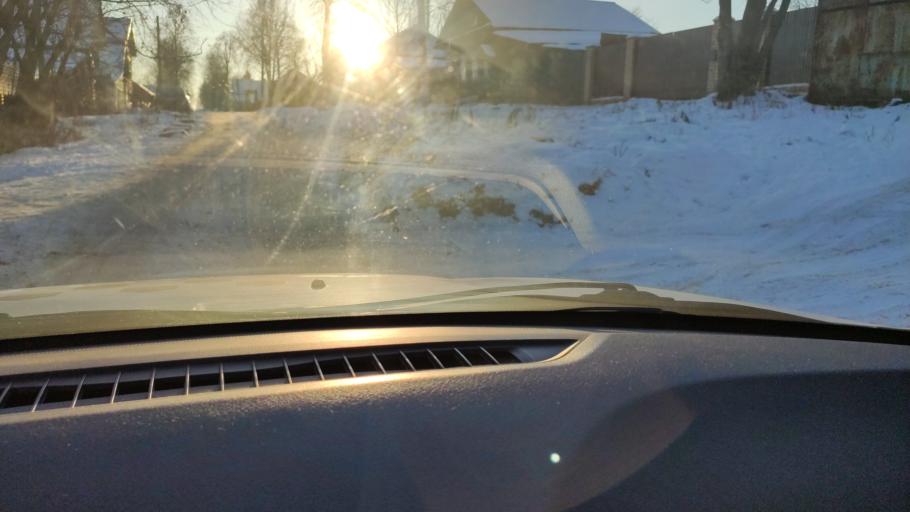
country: RU
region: Perm
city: Perm
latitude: 58.0316
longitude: 56.3317
